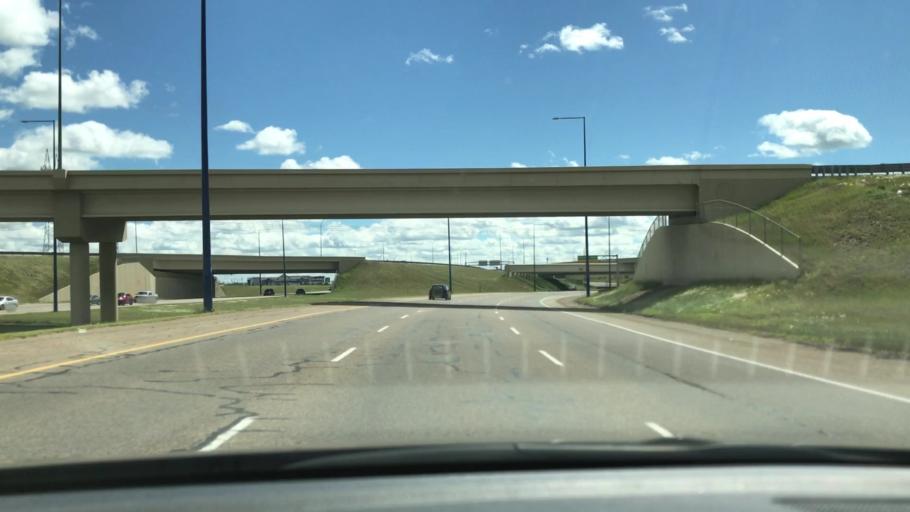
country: CA
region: Alberta
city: Beaumont
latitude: 53.4355
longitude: -113.4905
